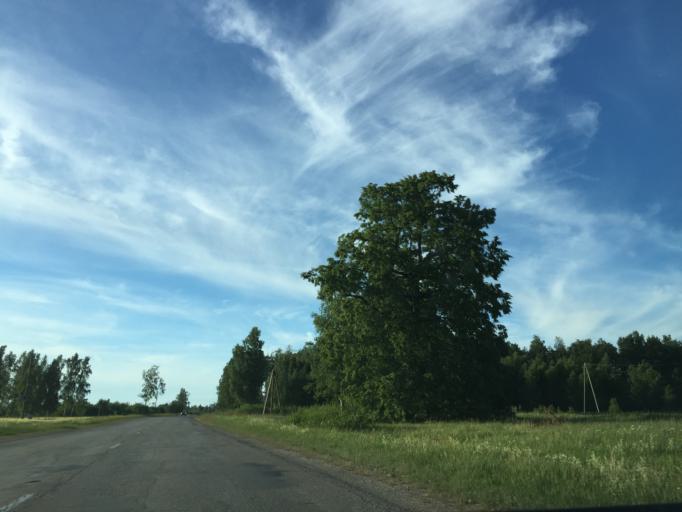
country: LV
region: Ventspils
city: Ventspils
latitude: 57.2927
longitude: 21.5642
